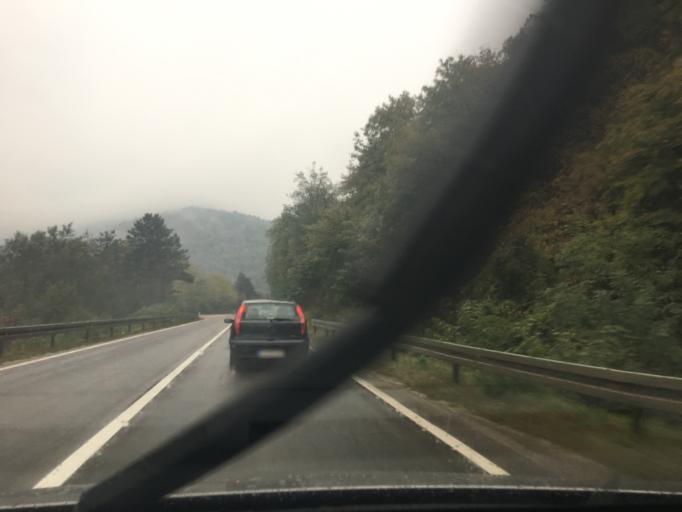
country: RS
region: Central Serbia
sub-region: Pcinjski Okrug
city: Vladicin Han
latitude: 42.7366
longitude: 22.0590
